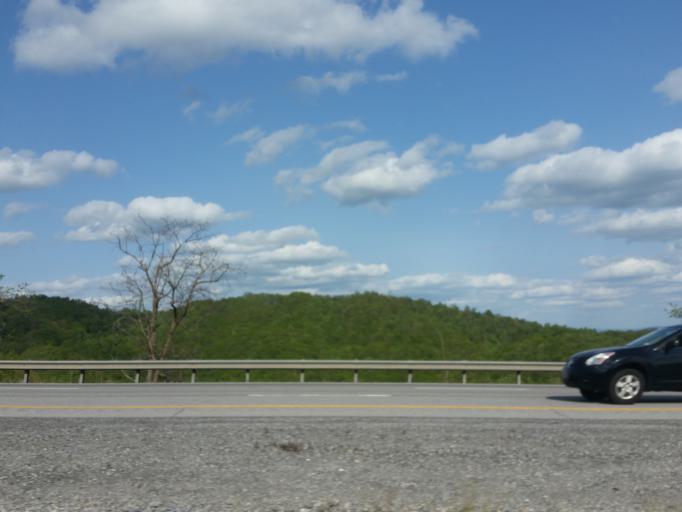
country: US
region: West Virginia
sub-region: Raleigh County
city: Shady Spring
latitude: 37.5597
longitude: -81.1134
